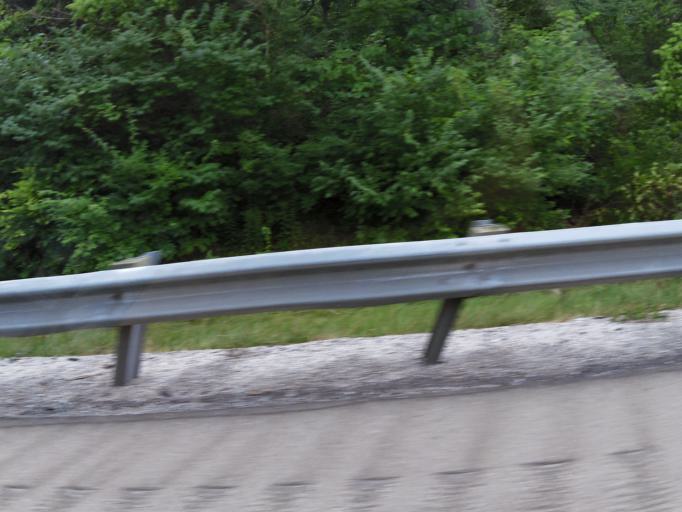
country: US
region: Kentucky
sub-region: Boone County
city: Walton
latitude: 38.8836
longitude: -84.6228
